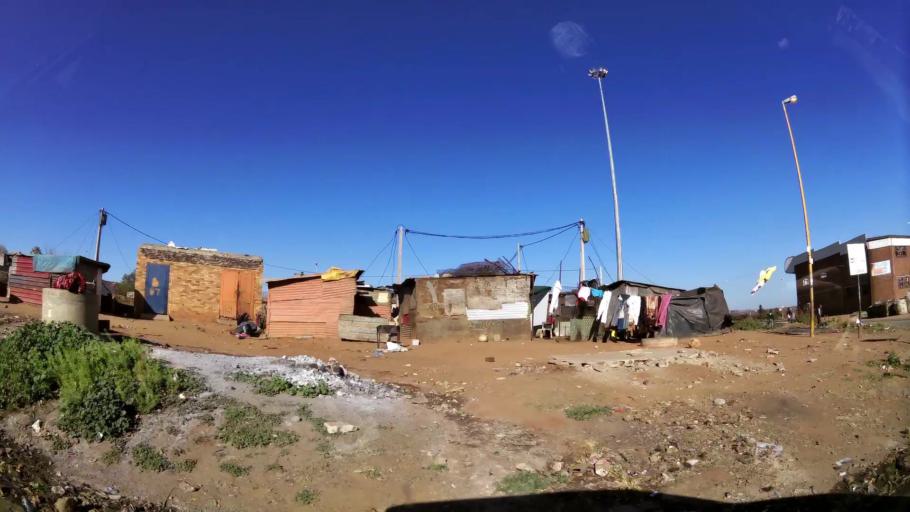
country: ZA
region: Gauteng
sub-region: Ekurhuleni Metropolitan Municipality
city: Tembisa
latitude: -26.0240
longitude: 28.2156
